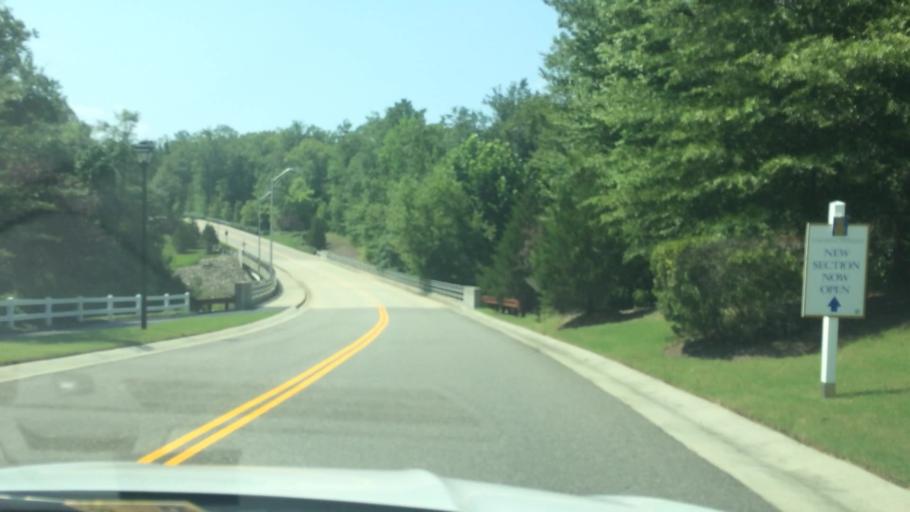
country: US
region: Virginia
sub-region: James City County
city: Williamsburg
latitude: 37.3411
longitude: -76.7778
